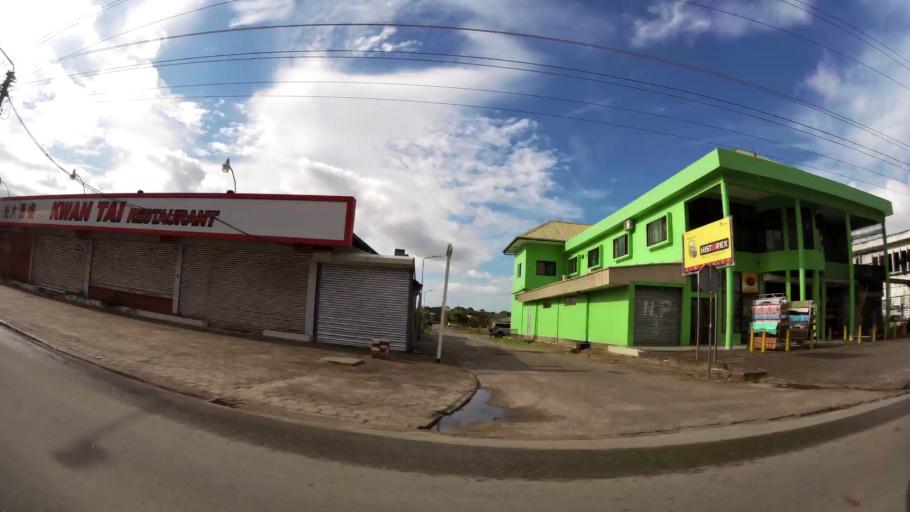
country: SR
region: Paramaribo
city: Paramaribo
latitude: 5.8430
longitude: -55.2119
